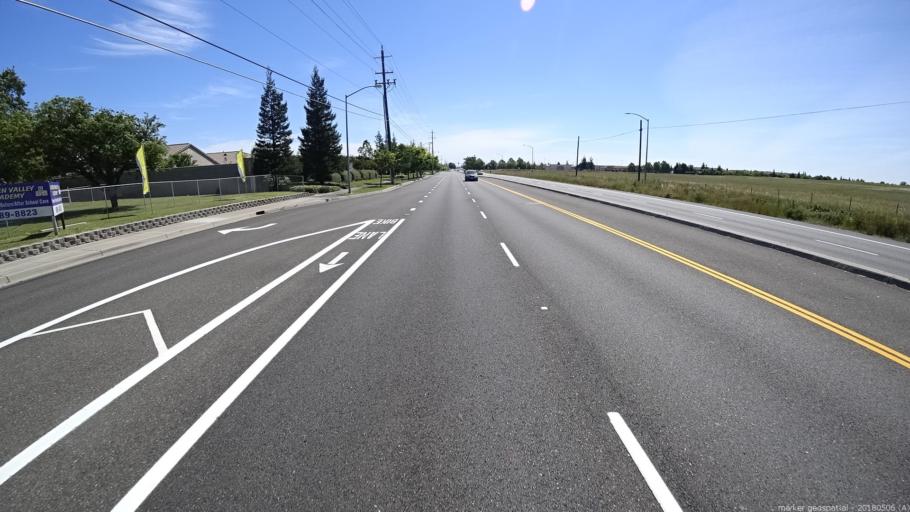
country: US
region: California
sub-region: Sacramento County
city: Laguna
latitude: 38.4381
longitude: -121.4127
